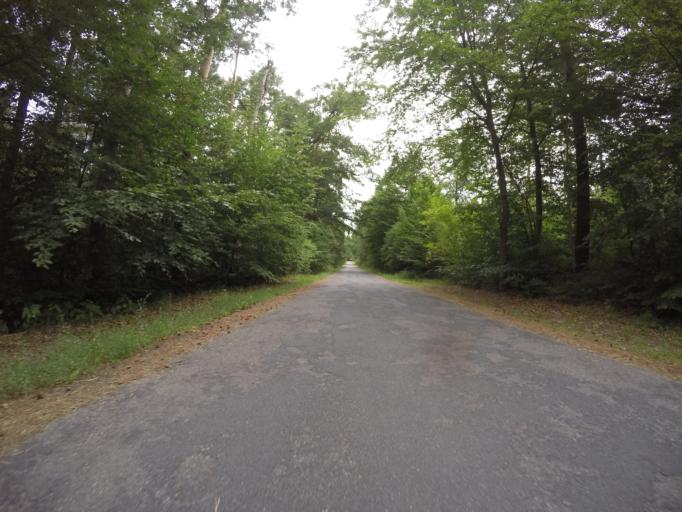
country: DE
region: Lower Saxony
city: Bleckede
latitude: 53.2691
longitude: 10.7156
